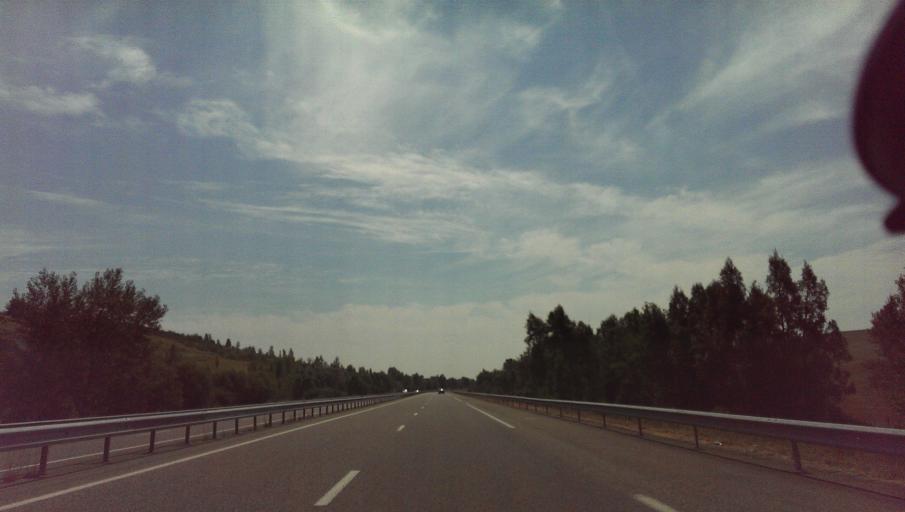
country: FR
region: Midi-Pyrenees
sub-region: Departement de la Haute-Garonne
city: Calmont
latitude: 43.3196
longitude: 1.6412
